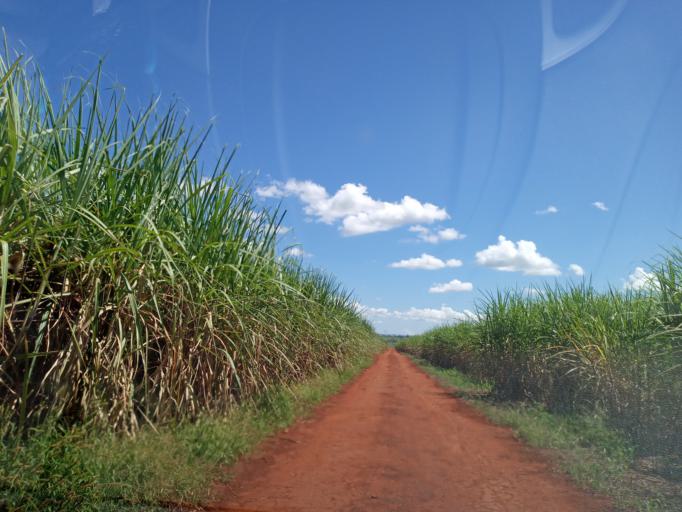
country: BR
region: Goias
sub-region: Itumbiara
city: Itumbiara
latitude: -18.4084
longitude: -49.1271
